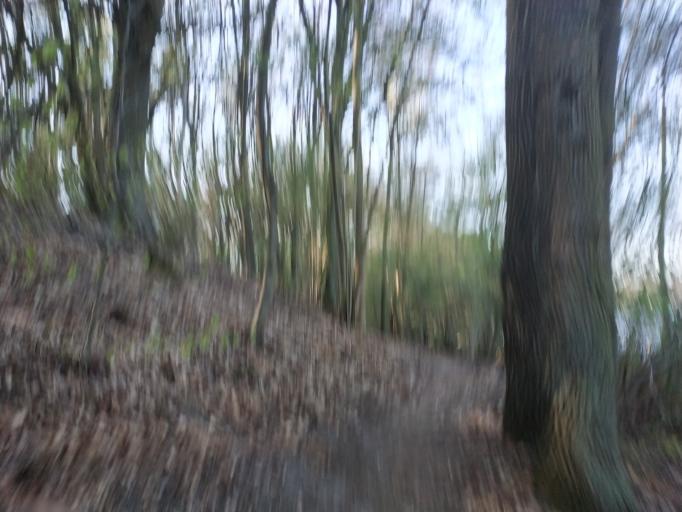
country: DE
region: Brandenburg
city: Strausberg
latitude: 52.5728
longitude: 13.8277
